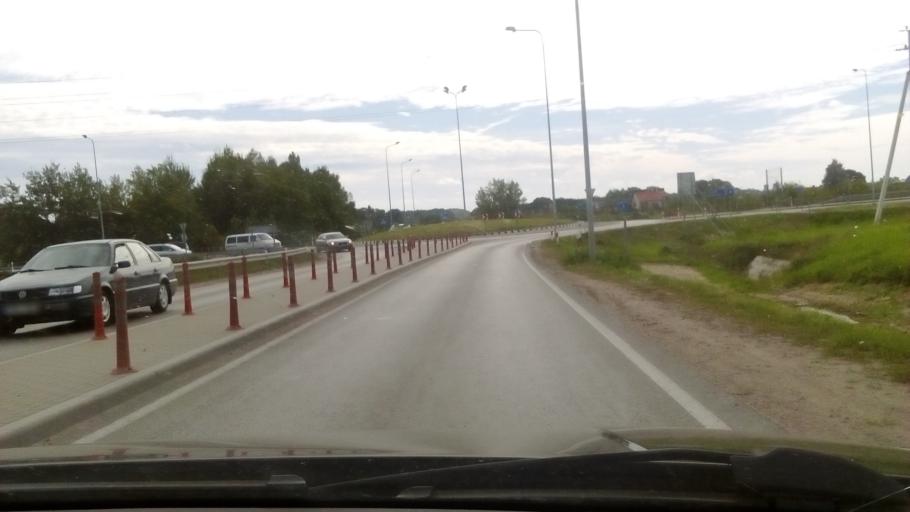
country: LT
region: Alytaus apskritis
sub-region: Alytus
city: Alytus
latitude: 54.3889
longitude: 23.9976
